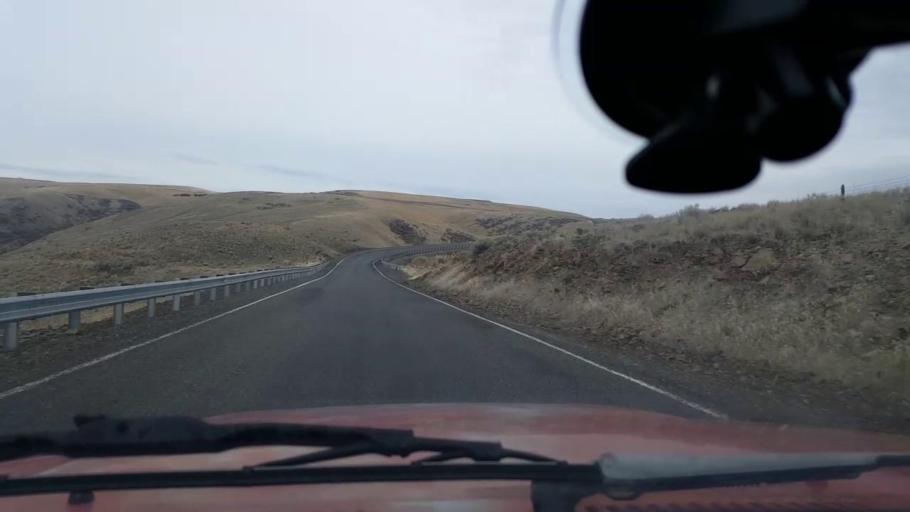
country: US
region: Washington
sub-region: Asotin County
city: Clarkston Heights-Vineland
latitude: 46.3330
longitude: -117.2952
